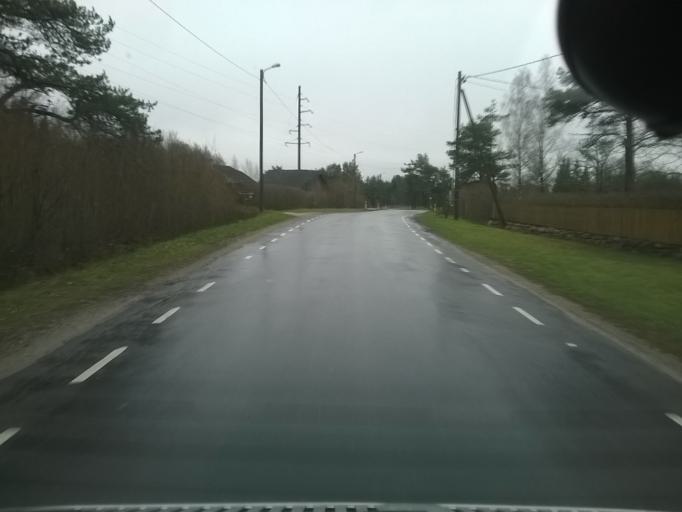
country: EE
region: Harju
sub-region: Nissi vald
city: Riisipere
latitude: 59.1153
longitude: 24.3096
